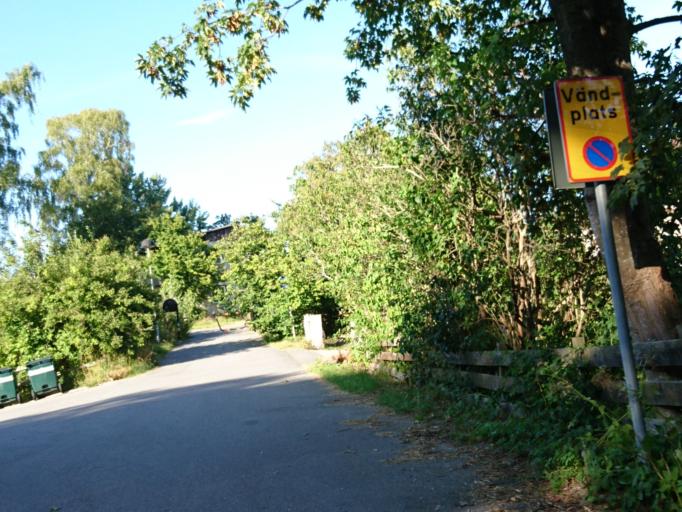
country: SE
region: Stockholm
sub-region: Huddinge Kommun
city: Segeltorp
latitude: 59.2739
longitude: 17.9471
